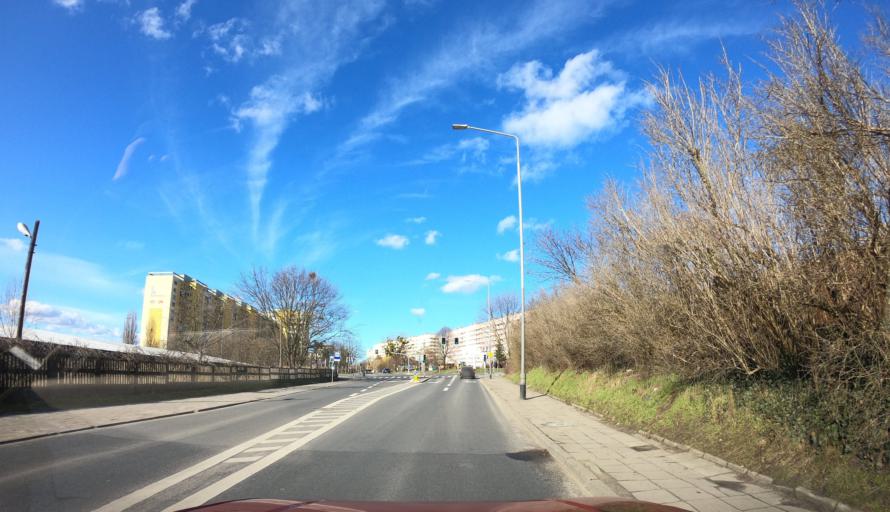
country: PL
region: West Pomeranian Voivodeship
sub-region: Szczecin
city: Szczecin
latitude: 53.4277
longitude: 14.5124
